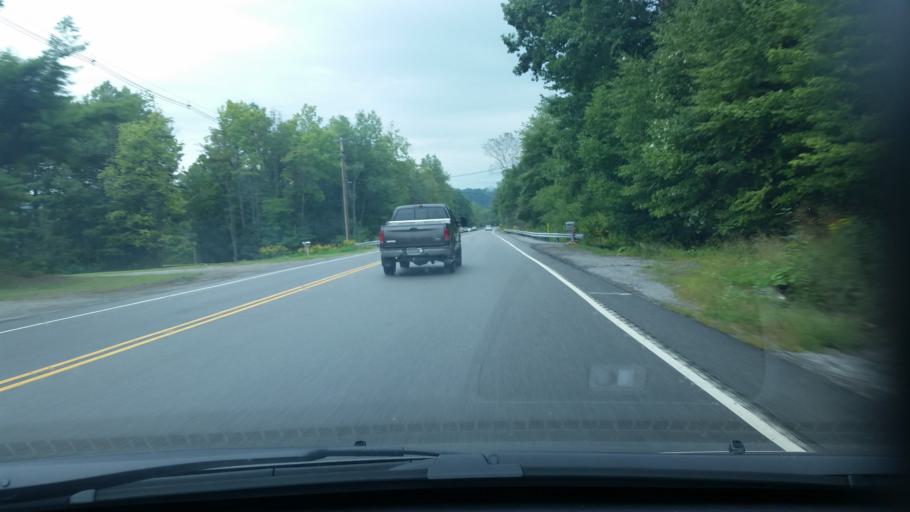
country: US
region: Pennsylvania
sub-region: Clearfield County
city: Shiloh
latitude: 41.0706
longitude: -78.3100
